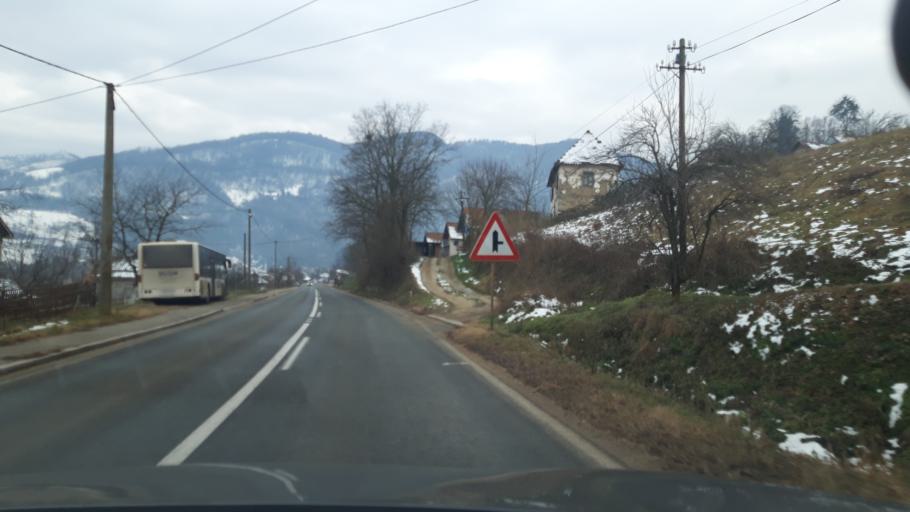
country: RS
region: Central Serbia
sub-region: Macvanski Okrug
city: Mali Zvornik
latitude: 44.2919
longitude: 19.1493
